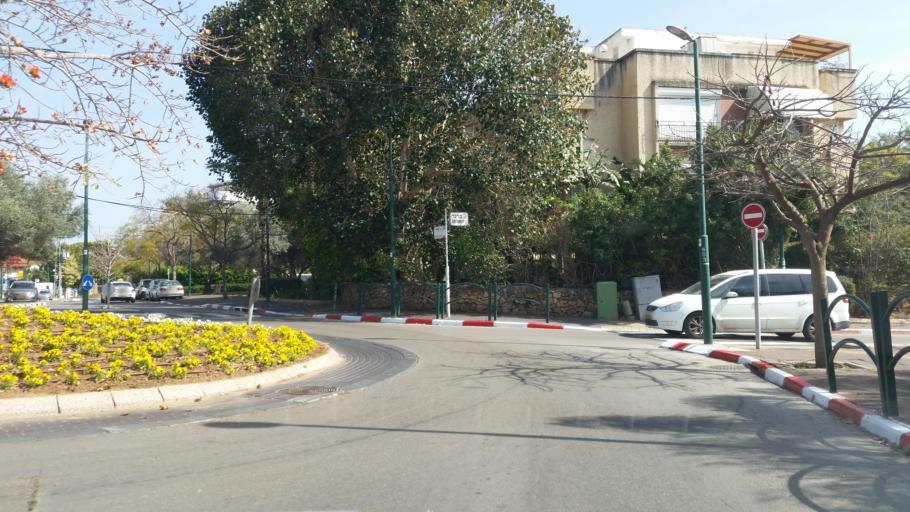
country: IL
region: Tel Aviv
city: Ramat HaSharon
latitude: 32.1591
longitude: 34.8502
